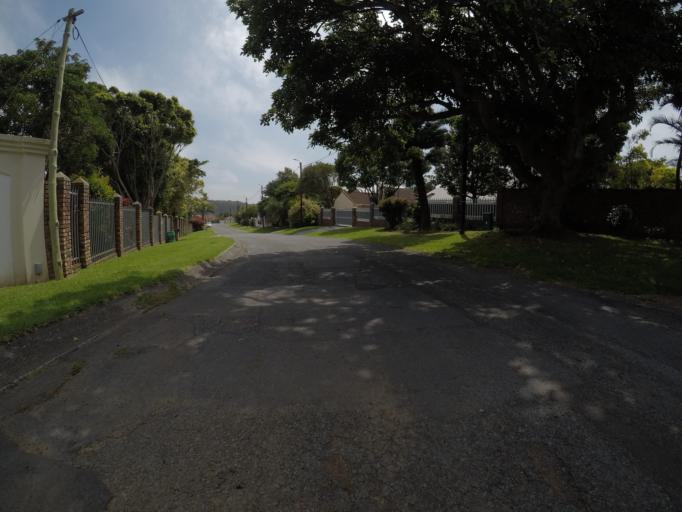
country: ZA
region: Eastern Cape
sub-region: Buffalo City Metropolitan Municipality
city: East London
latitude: -32.9363
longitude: 28.0245
